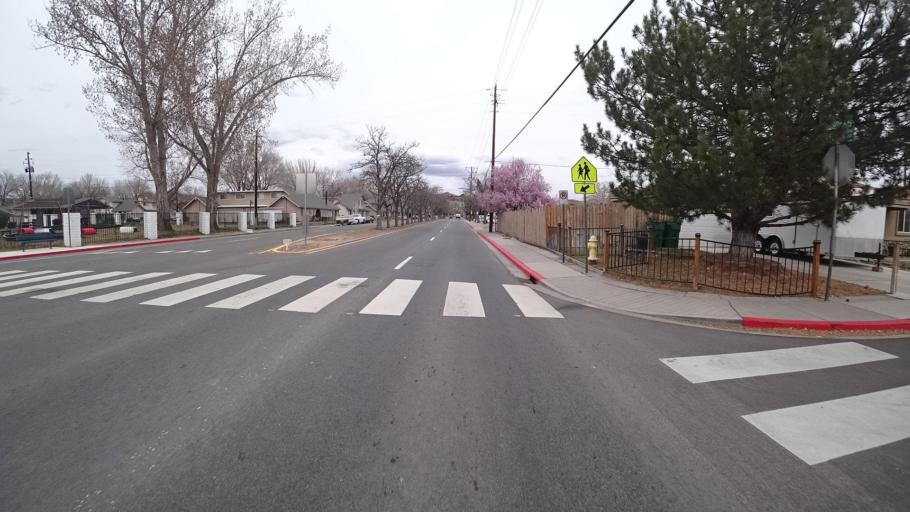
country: US
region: Nevada
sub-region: Washoe County
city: Sparks
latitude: 39.5508
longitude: -119.7619
